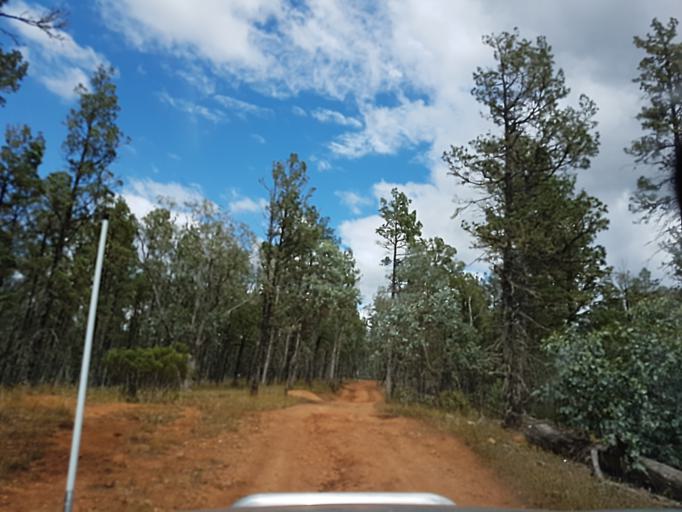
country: AU
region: New South Wales
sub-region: Snowy River
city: Jindabyne
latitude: -36.9297
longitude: 148.3953
